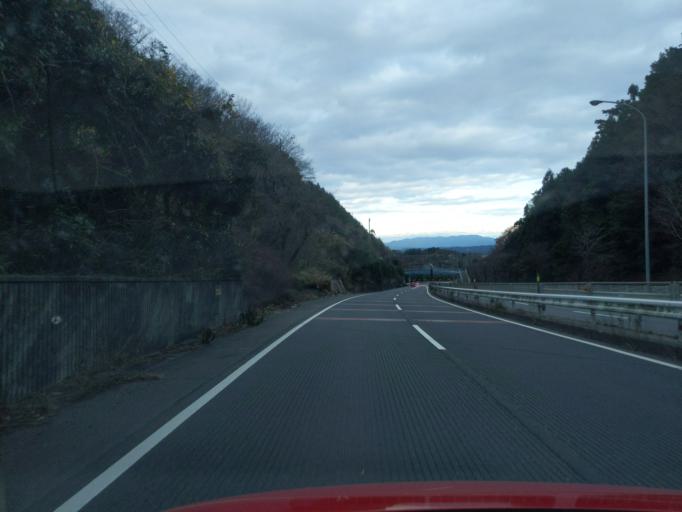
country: JP
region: Gifu
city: Tajimi
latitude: 35.3306
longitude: 137.0766
